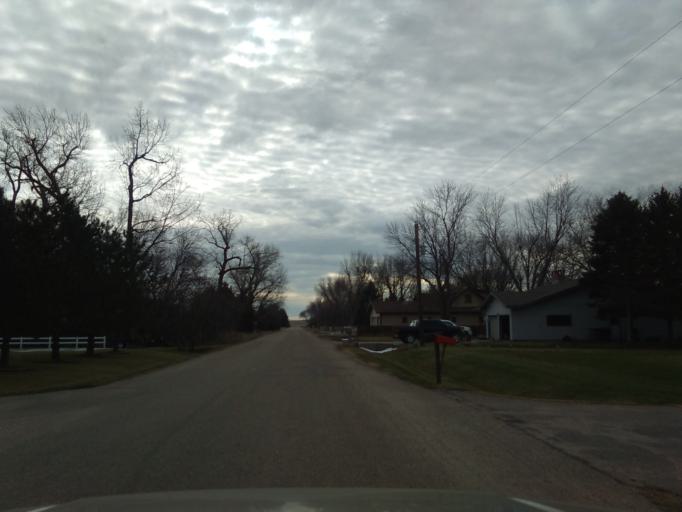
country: US
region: Nebraska
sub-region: Hall County
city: Grand Island
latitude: 40.7763
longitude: -98.4119
